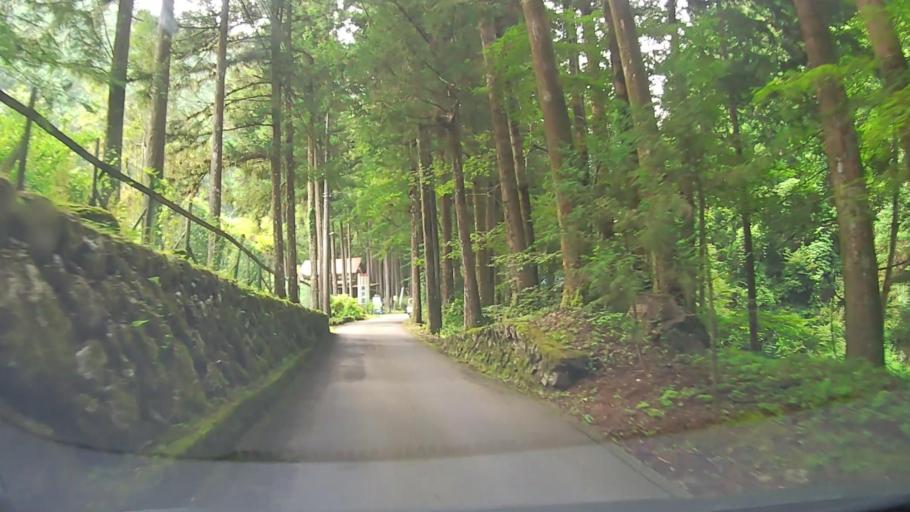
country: JP
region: Tokyo
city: Itsukaichi
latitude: 35.7504
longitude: 139.1162
